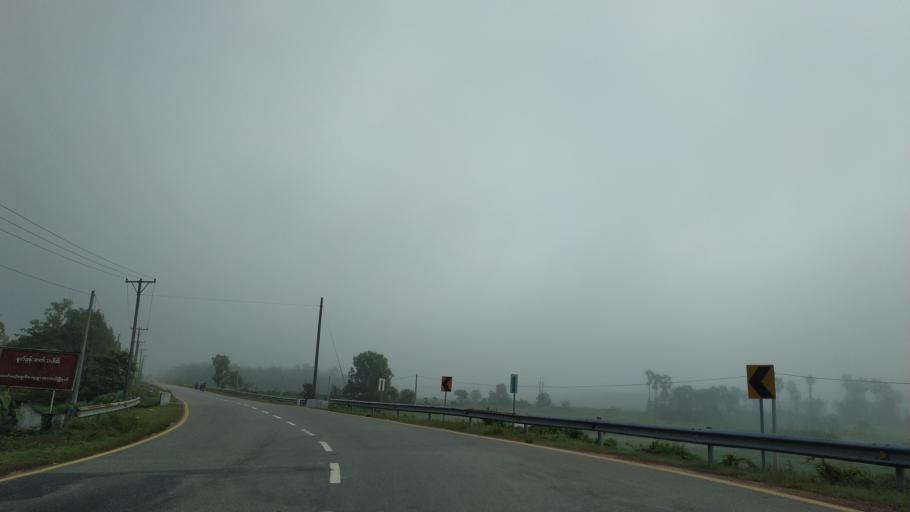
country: MM
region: Tanintharyi
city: Dawei
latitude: 14.1624
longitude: 98.2083
